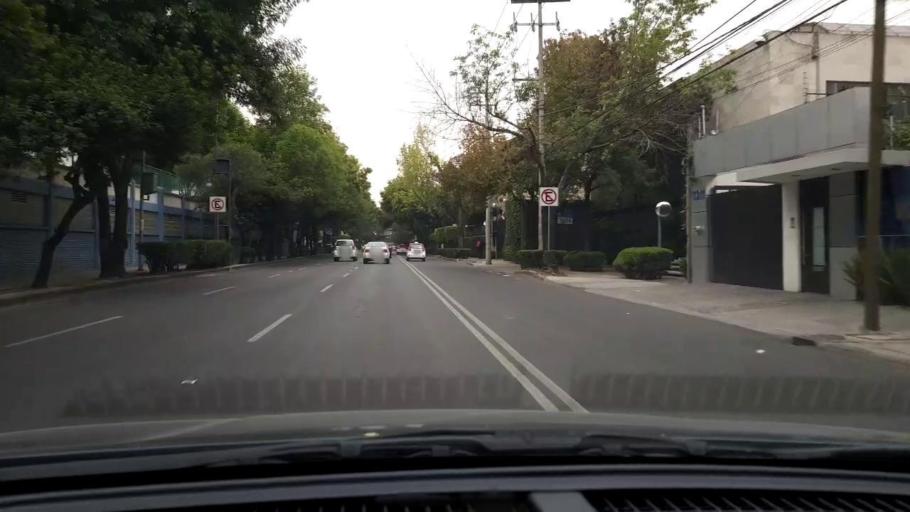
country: MX
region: Mexico City
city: Colonia del Valle
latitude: 19.3760
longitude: -99.1699
